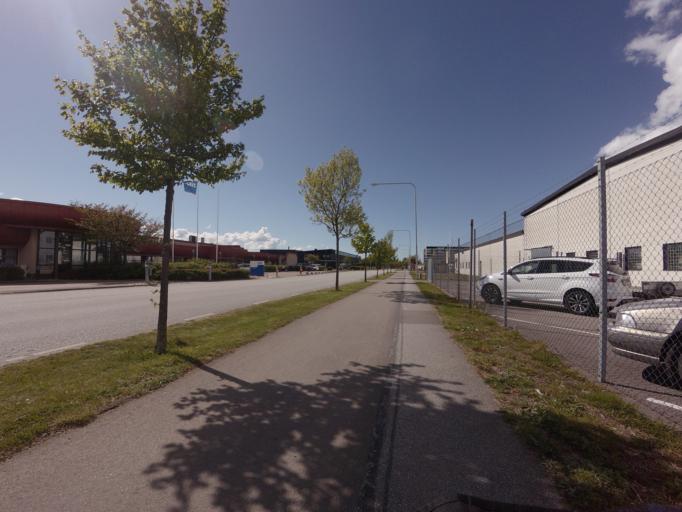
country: SE
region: Skane
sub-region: Landskrona
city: Landskrona
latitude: 55.8881
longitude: 12.8533
